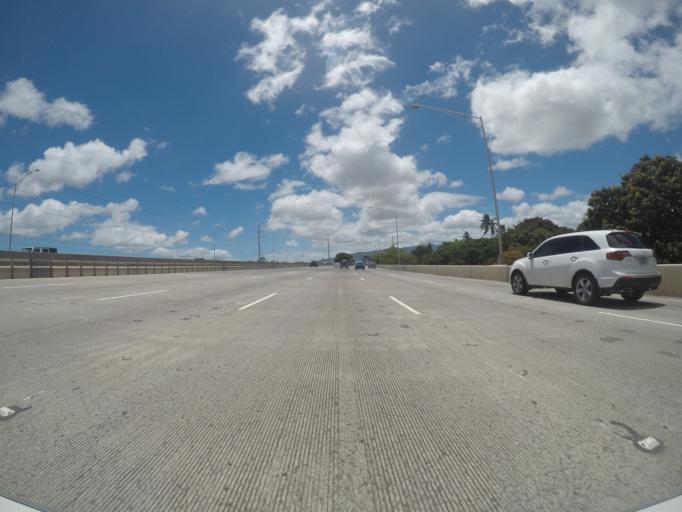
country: US
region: Hawaii
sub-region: Honolulu County
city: Pearl City, Manana
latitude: 21.3899
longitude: -157.9665
